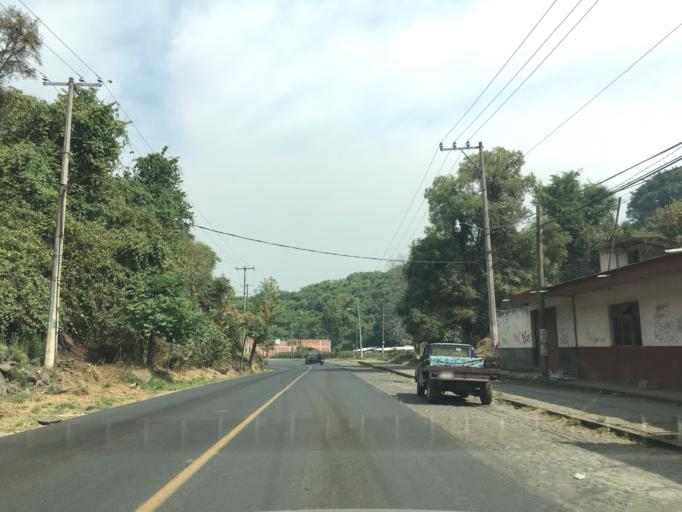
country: MX
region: Michoacan
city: Nuevo San Juan Parangaricutiro
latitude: 19.4139
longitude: -102.1234
